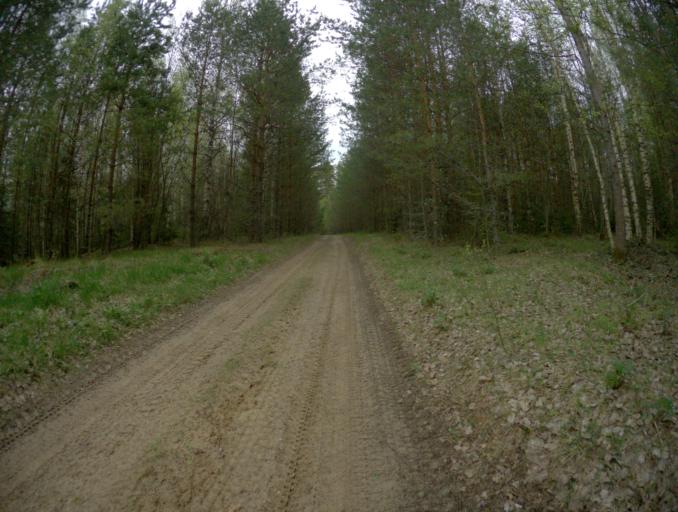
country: RU
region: Vladimir
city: Golovino
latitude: 55.9010
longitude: 40.4365
